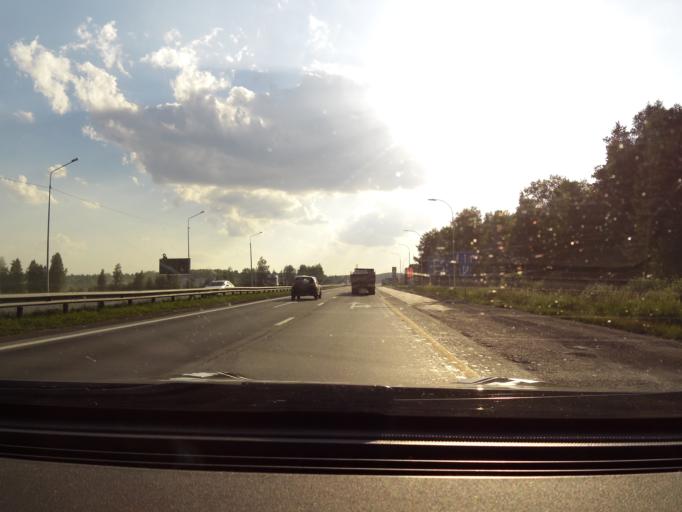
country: RU
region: Sverdlovsk
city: Severka
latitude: 56.8380
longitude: 60.1631
